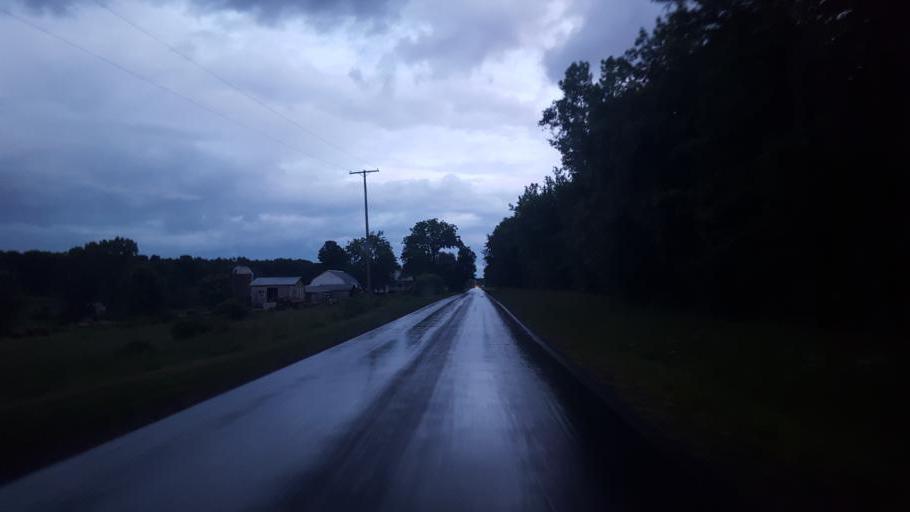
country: US
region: New York
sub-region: Wayne County
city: Clyde
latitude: 43.0500
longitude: -76.8840
